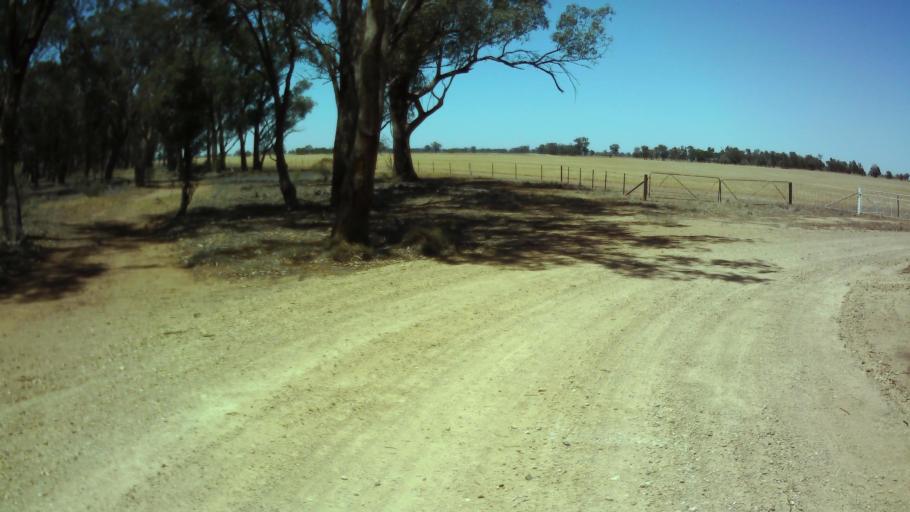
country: AU
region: New South Wales
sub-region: Weddin
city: Grenfell
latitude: -34.0446
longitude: 148.0120
